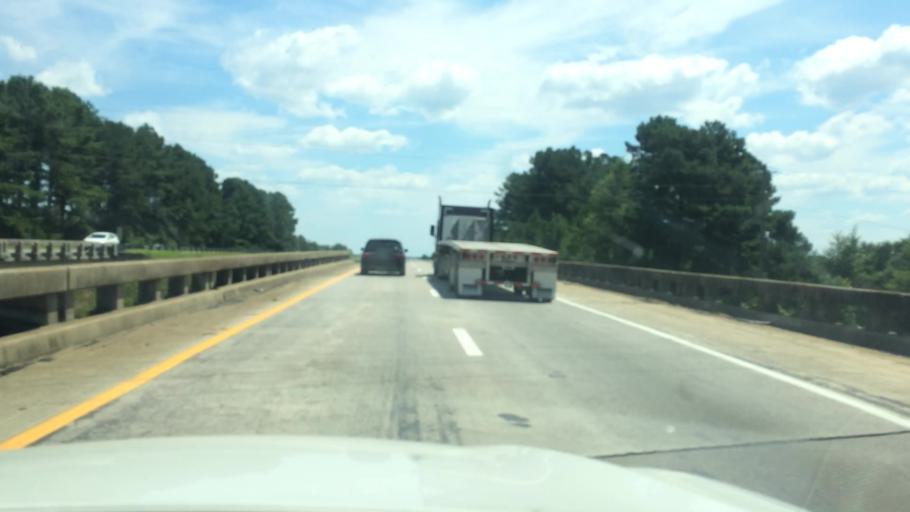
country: US
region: South Carolina
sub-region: Aiken County
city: Aiken
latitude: 33.6390
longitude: -81.7409
